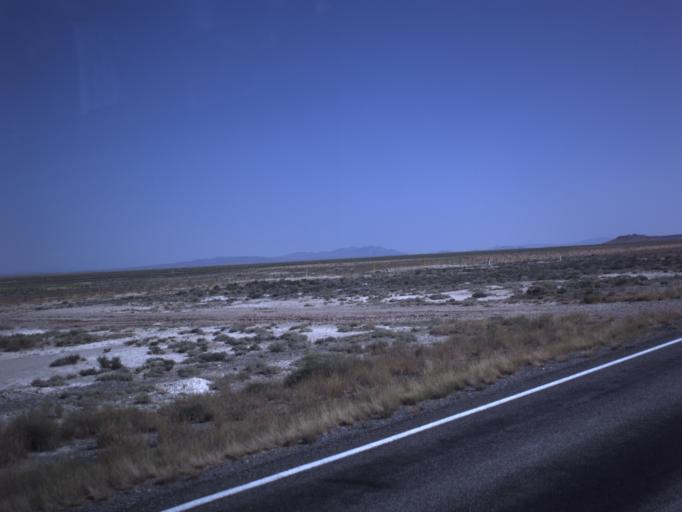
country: US
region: Utah
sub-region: Millard County
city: Delta
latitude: 39.0450
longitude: -112.7696
